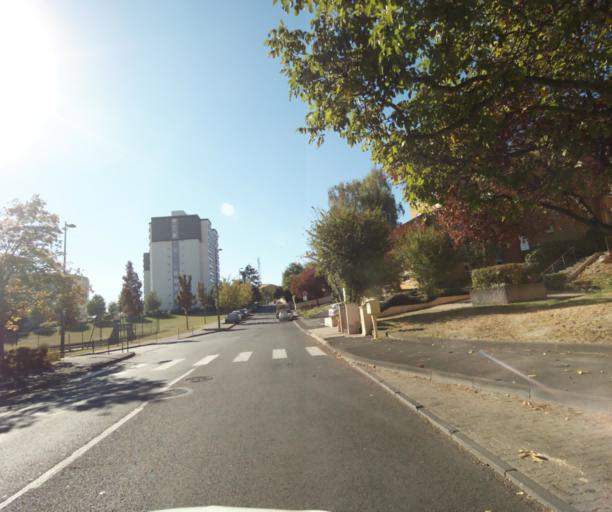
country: FR
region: Auvergne
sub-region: Departement du Puy-de-Dome
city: Cebazat
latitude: 45.8124
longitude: 3.0996
